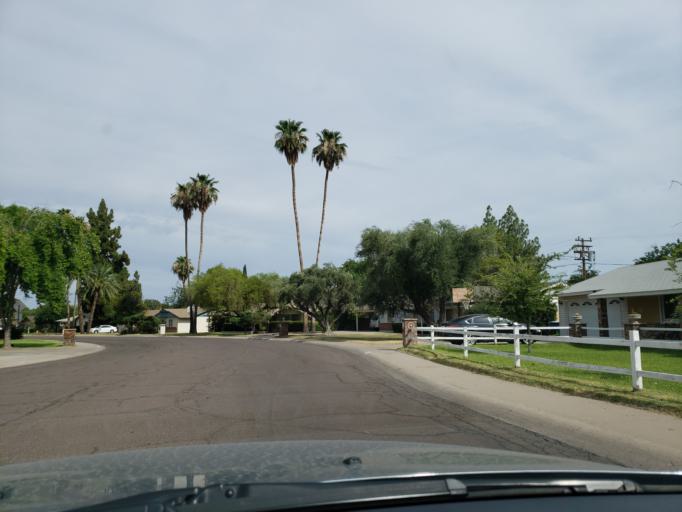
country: US
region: Arizona
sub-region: Maricopa County
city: Glendale
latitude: 33.5605
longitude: -112.0788
